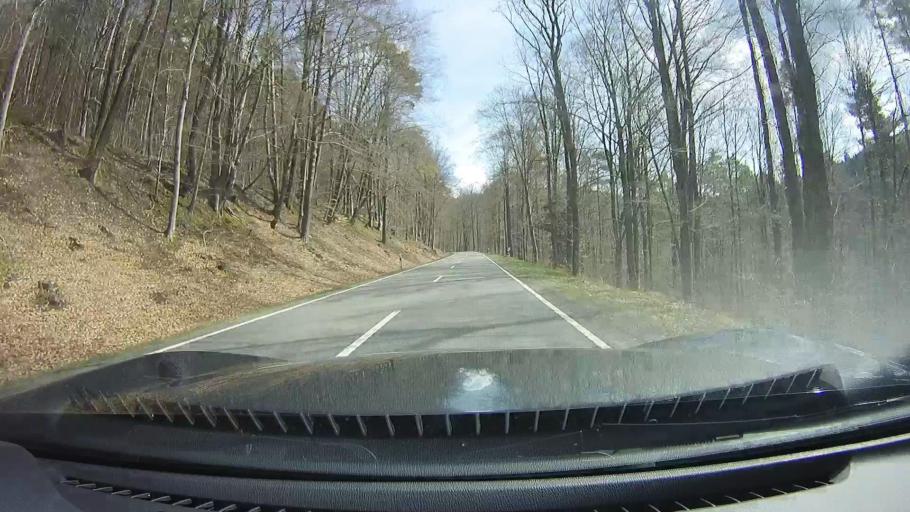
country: DE
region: Hesse
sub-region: Regierungsbezirk Darmstadt
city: Beerfelden
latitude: 49.5837
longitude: 9.0100
